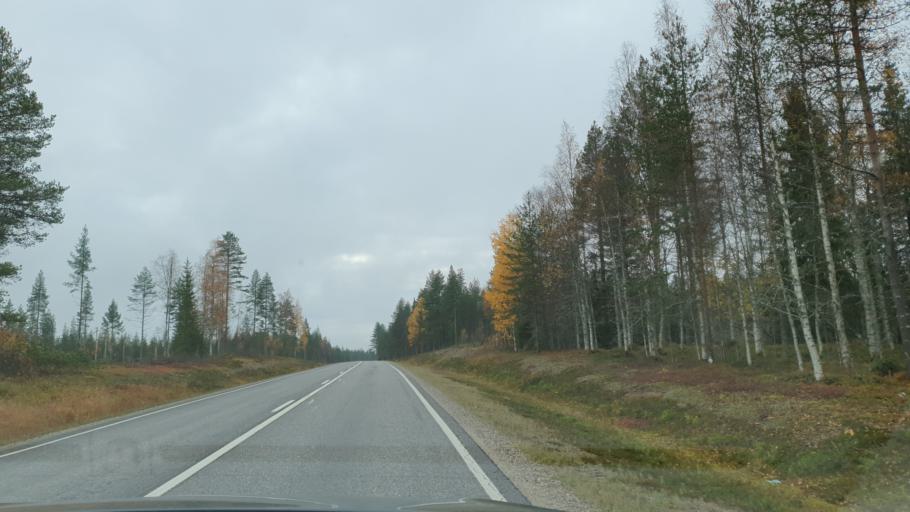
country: FI
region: Lapland
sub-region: Rovaniemi
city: Ranua
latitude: 66.0382
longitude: 26.3390
